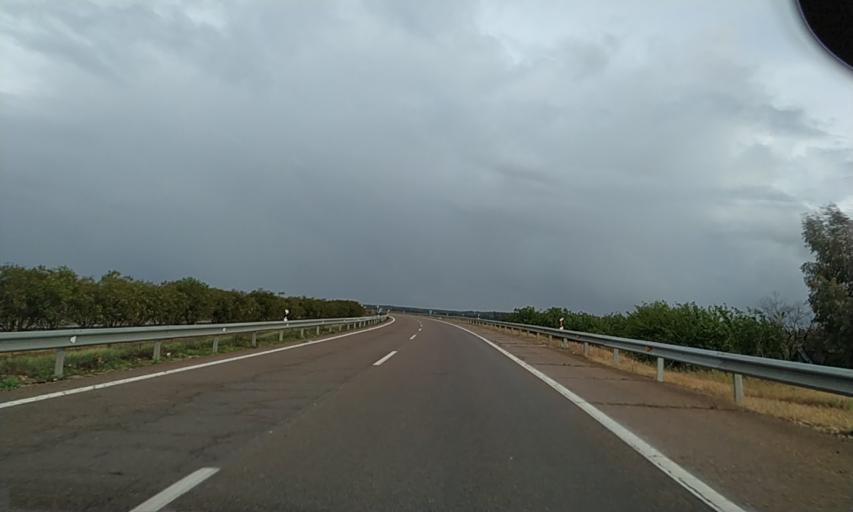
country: ES
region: Extremadura
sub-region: Provincia de Badajoz
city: Badajoz
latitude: 38.9115
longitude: -6.9480
